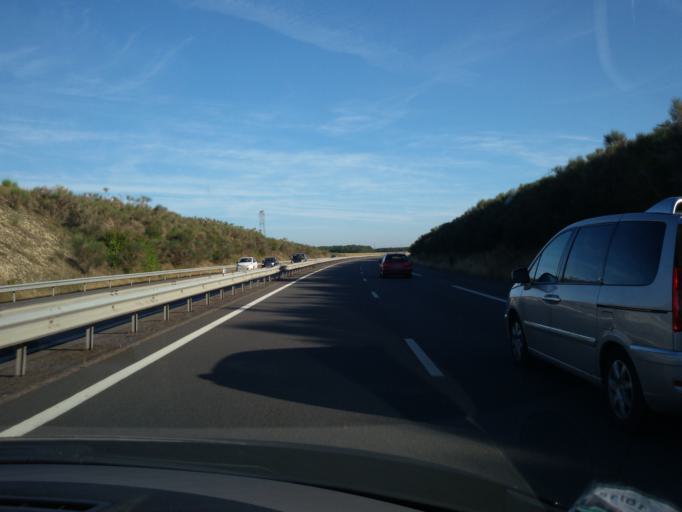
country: FR
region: Centre
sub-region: Departement du Cher
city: Trouy
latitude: 47.0138
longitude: 2.3837
